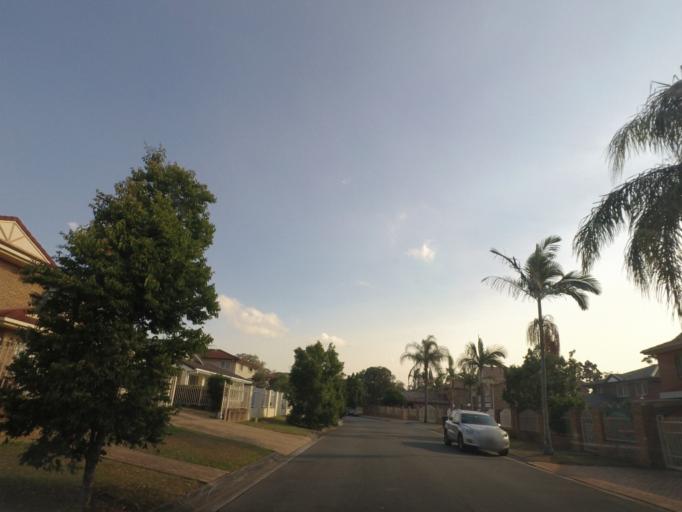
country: AU
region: Queensland
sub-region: Brisbane
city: Robertson
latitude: -27.5605
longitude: 153.0562
